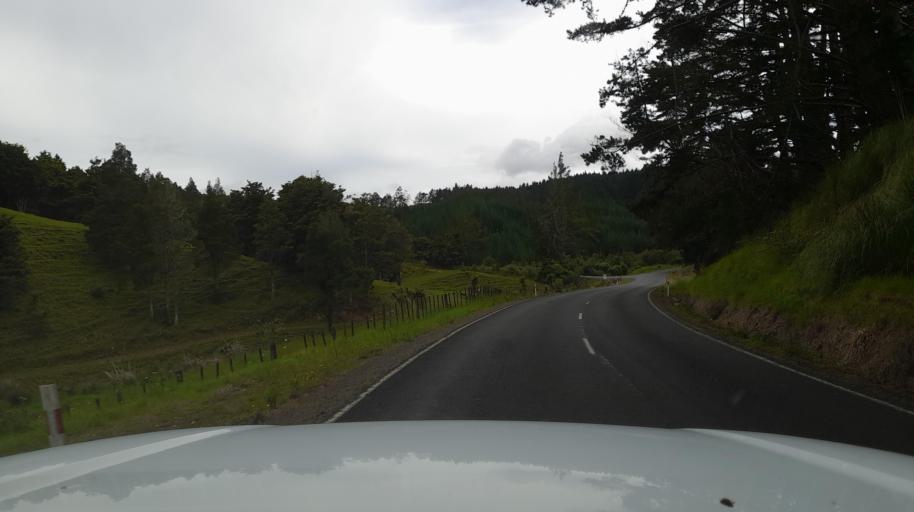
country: NZ
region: Northland
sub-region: Far North District
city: Kaitaia
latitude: -35.2663
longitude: 173.2927
